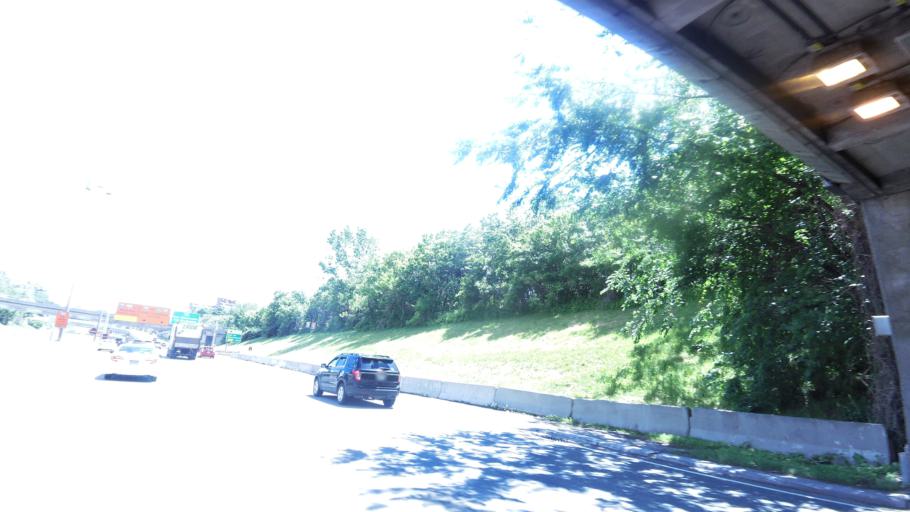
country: CA
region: Quebec
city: Saint-Raymond
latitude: 45.4763
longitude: -73.6173
